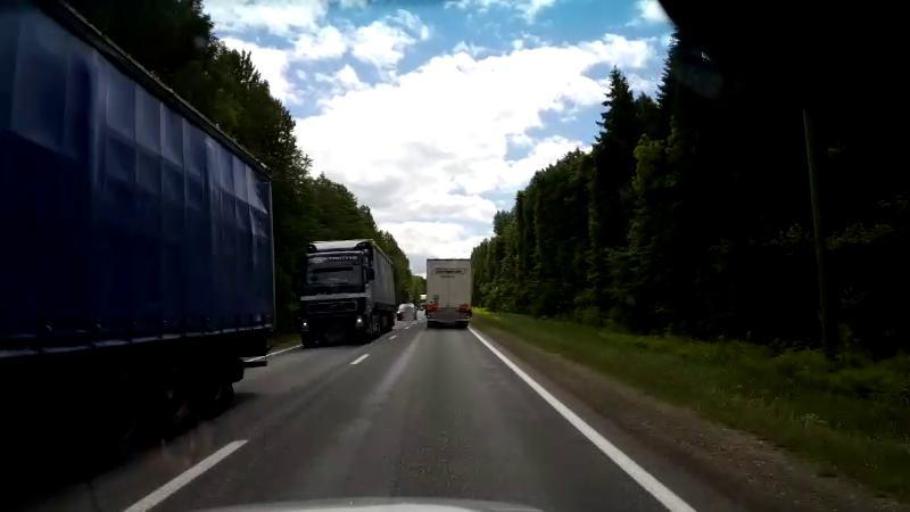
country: LV
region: Salacgrivas
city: Salacgriva
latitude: 57.5950
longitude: 24.4147
